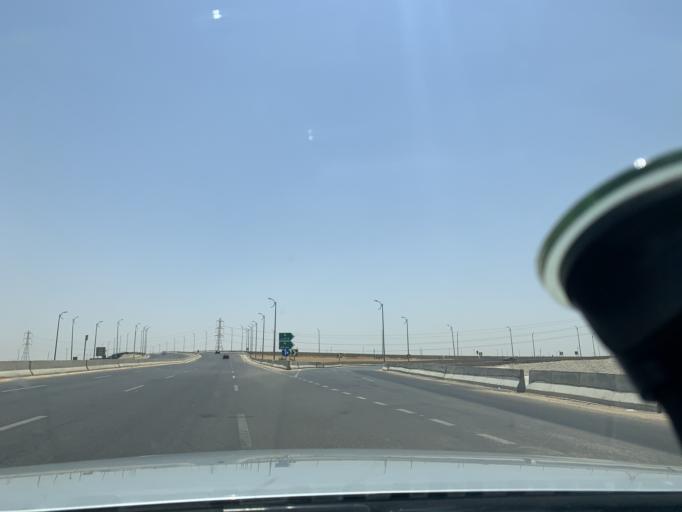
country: EG
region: Muhafazat al Qahirah
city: Halwan
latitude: 29.9703
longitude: 31.4694
